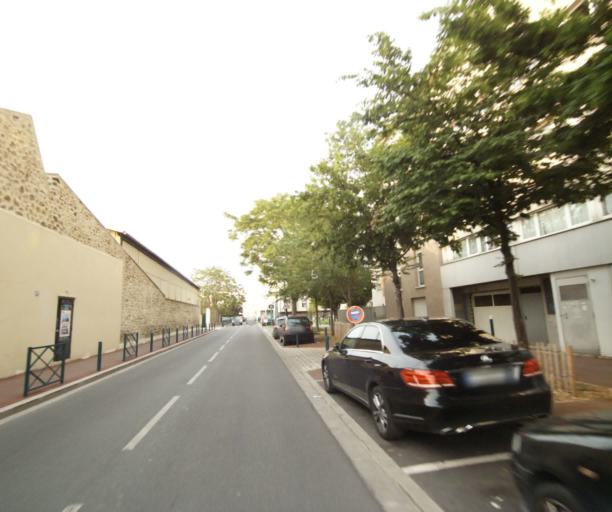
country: FR
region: Ile-de-France
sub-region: Departement des Hauts-de-Seine
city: Gennevilliers
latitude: 48.9187
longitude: 2.3028
